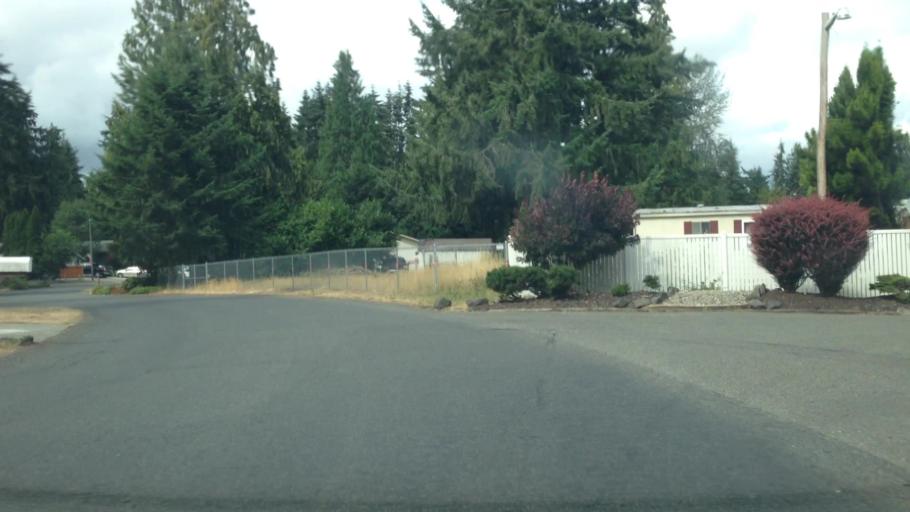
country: US
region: Washington
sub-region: Pierce County
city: South Hill
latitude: 47.1148
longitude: -122.2988
